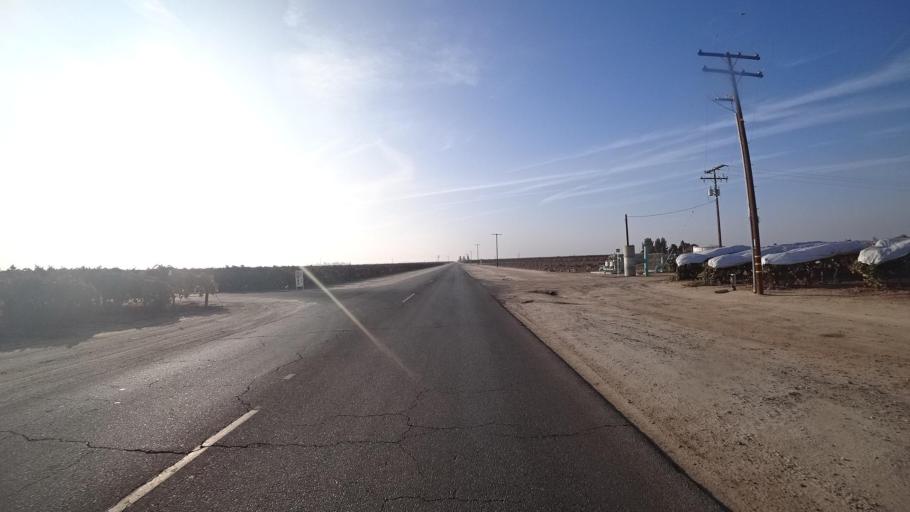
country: US
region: California
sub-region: Kern County
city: Delano
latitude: 35.7726
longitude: -119.1875
